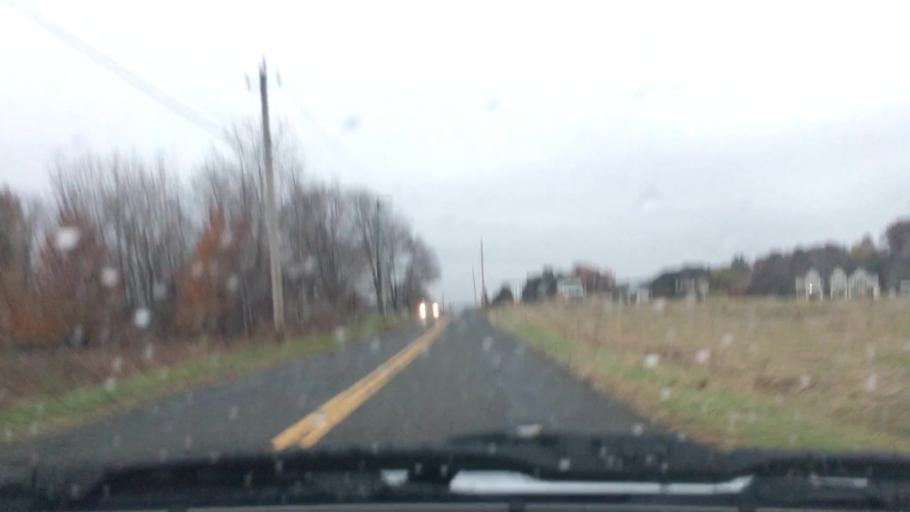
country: US
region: Massachusetts
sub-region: Hampden County
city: Southwick
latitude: 42.0942
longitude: -72.7776
